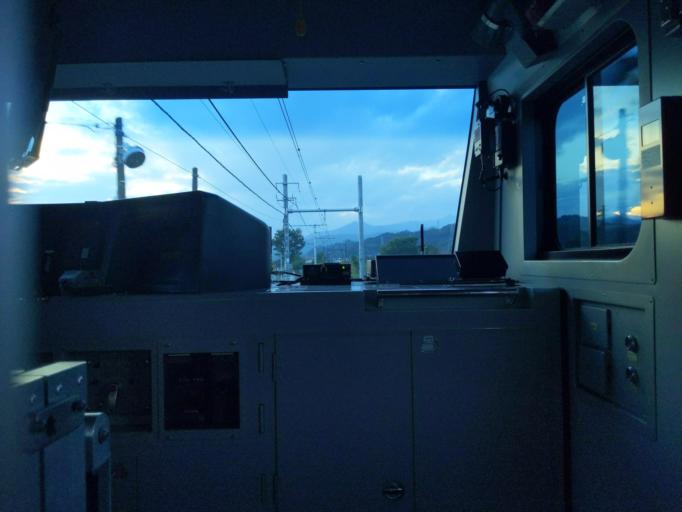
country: JP
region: Tokyo
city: Itsukaichi
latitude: 35.7304
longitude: 139.2631
